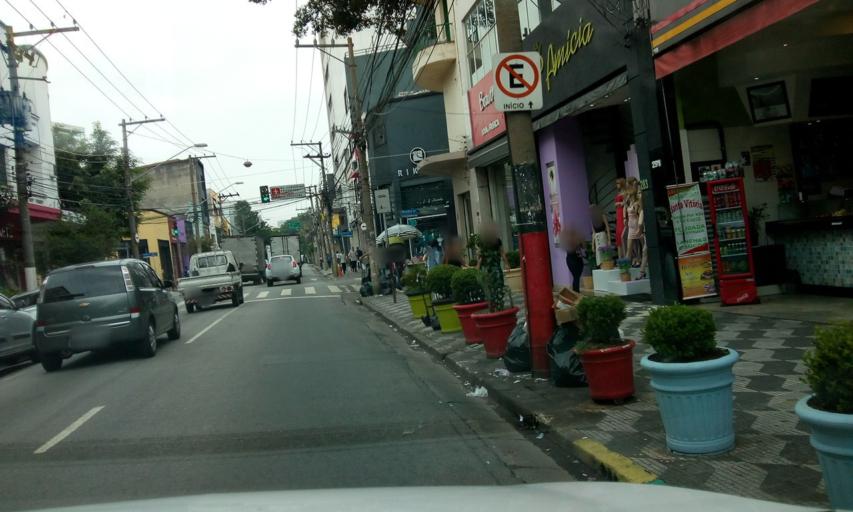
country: BR
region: Sao Paulo
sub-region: Sao Paulo
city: Sao Paulo
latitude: -23.5340
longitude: -46.6146
